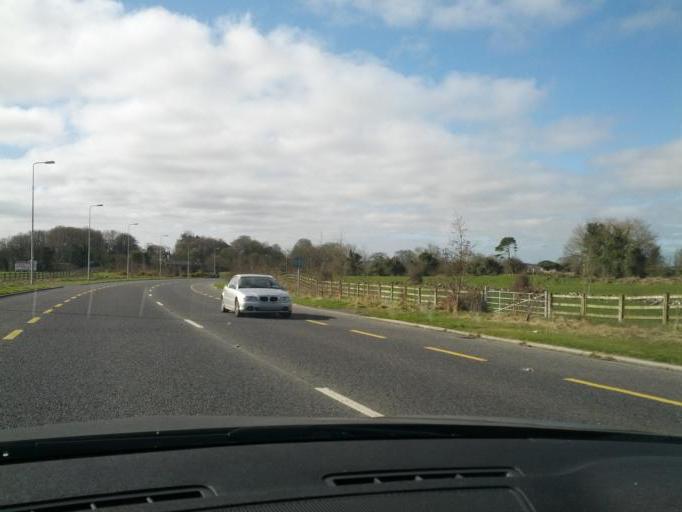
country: IE
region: Connaught
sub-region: County Galway
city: Ballinasloe
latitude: 53.3239
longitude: -8.1746
